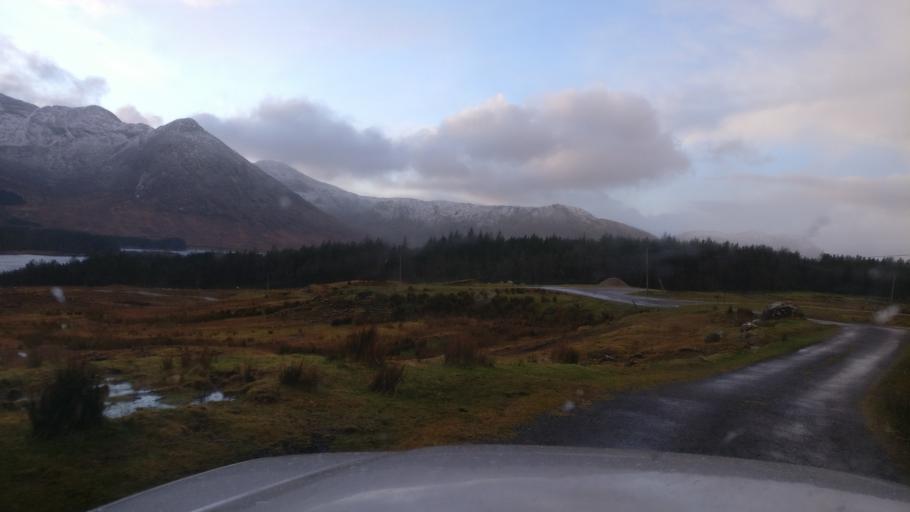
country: IE
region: Connaught
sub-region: County Galway
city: Clifden
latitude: 53.5182
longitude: -9.7312
